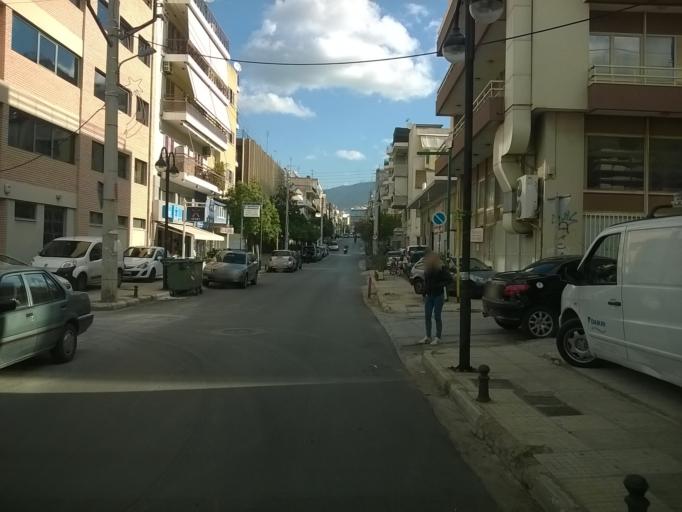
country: GR
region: Attica
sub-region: Nomarchia Athinas
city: Agios Dimitrios
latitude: 37.9319
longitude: 23.7415
